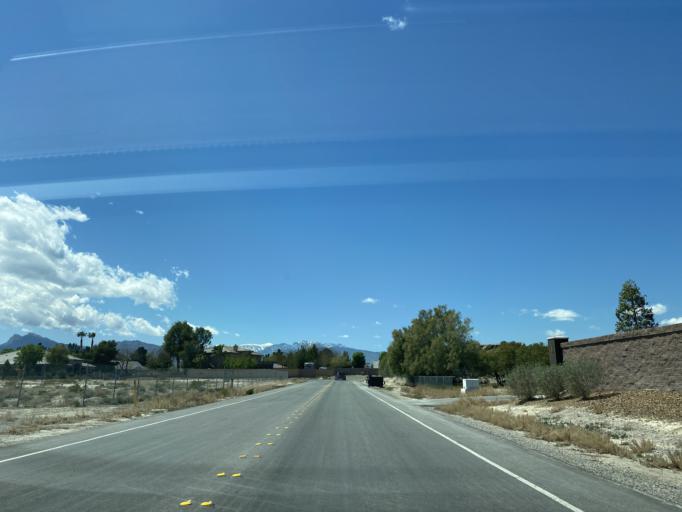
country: US
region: Nevada
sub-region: Clark County
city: North Las Vegas
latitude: 36.3110
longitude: -115.2363
